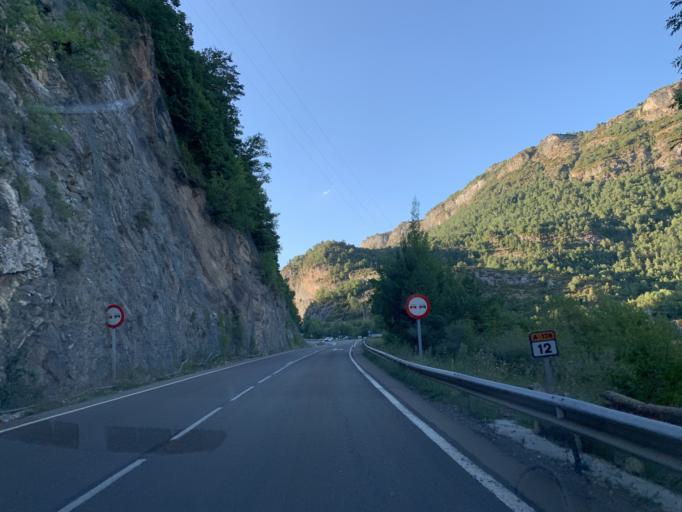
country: ES
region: Aragon
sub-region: Provincia de Huesca
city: Hoz de Jaca
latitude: 42.7252
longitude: -0.3069
